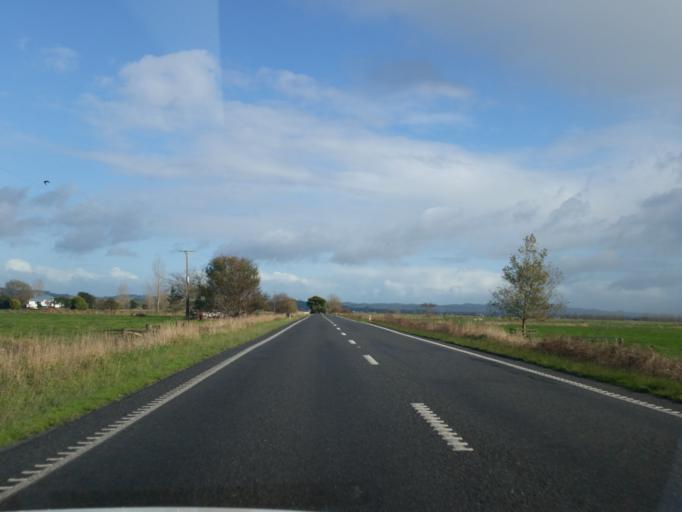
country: NZ
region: Waikato
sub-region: Hauraki District
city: Ngatea
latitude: -37.2761
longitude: 175.4695
